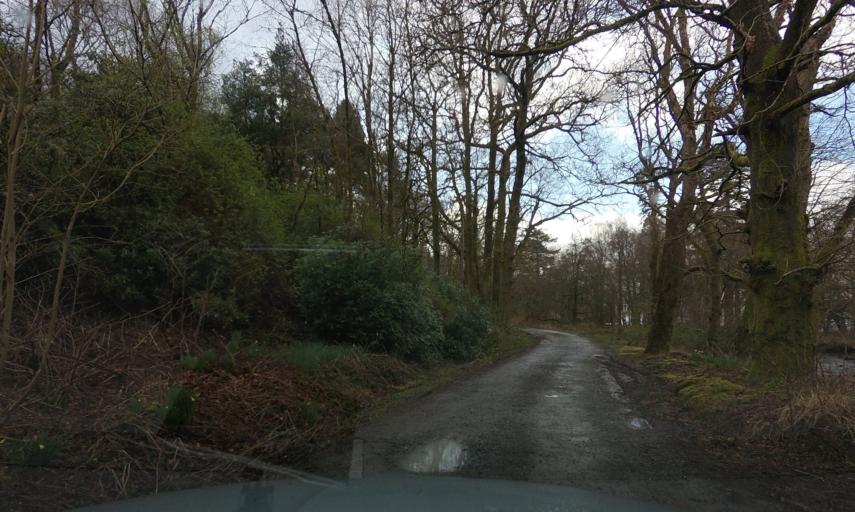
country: GB
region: Scotland
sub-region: West Dunbartonshire
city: Balloch
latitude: 56.1574
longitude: -4.6417
